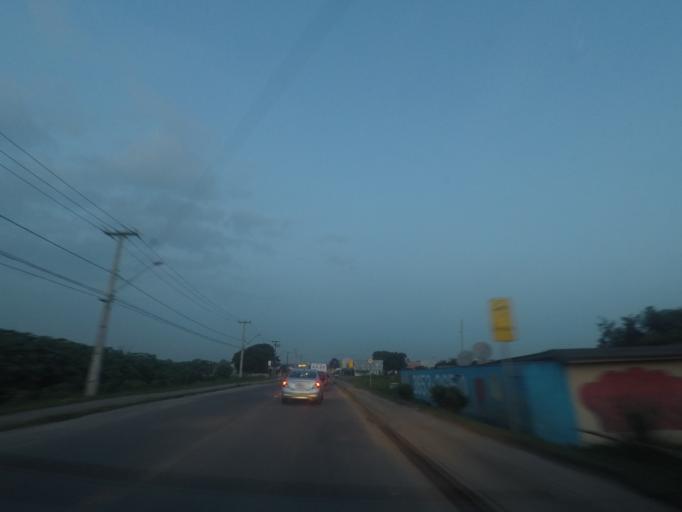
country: BR
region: Parana
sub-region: Pinhais
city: Pinhais
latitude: -25.4563
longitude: -49.1659
